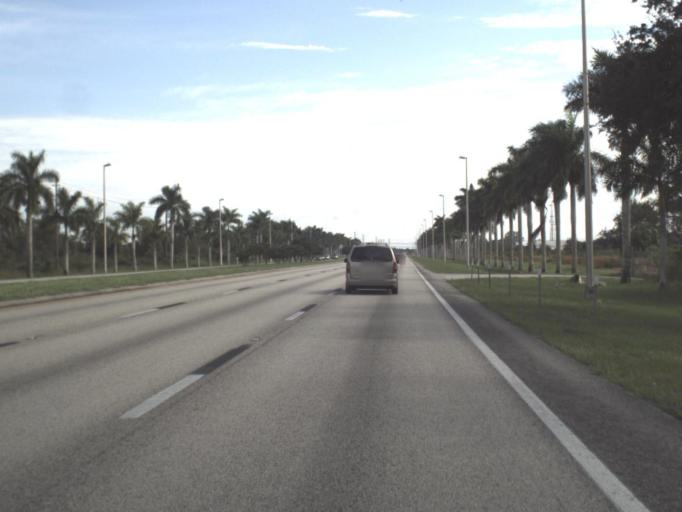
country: US
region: Florida
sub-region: Lee County
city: Tice
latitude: 26.6901
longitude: -81.7879
